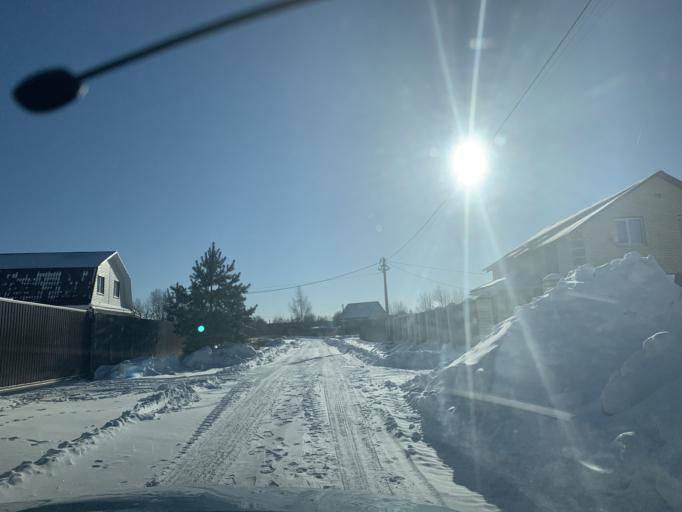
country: RU
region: Jaroslavl
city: Tunoshna
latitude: 57.6637
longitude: 40.0666
